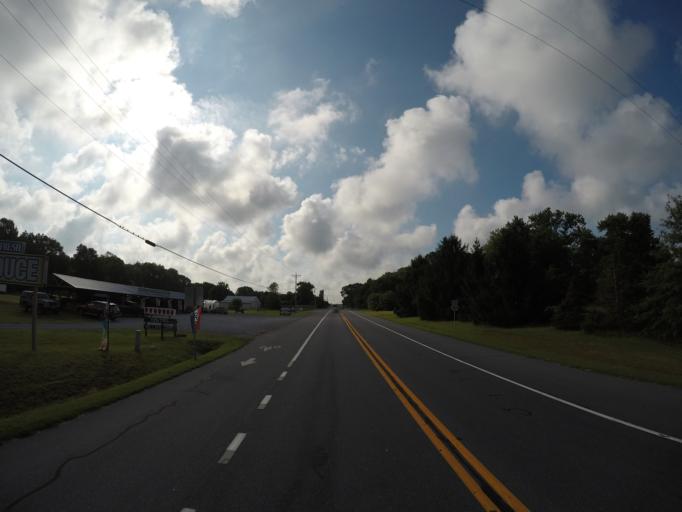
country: US
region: Delaware
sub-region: Sussex County
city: Bridgeville
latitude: 38.7928
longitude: -75.6915
